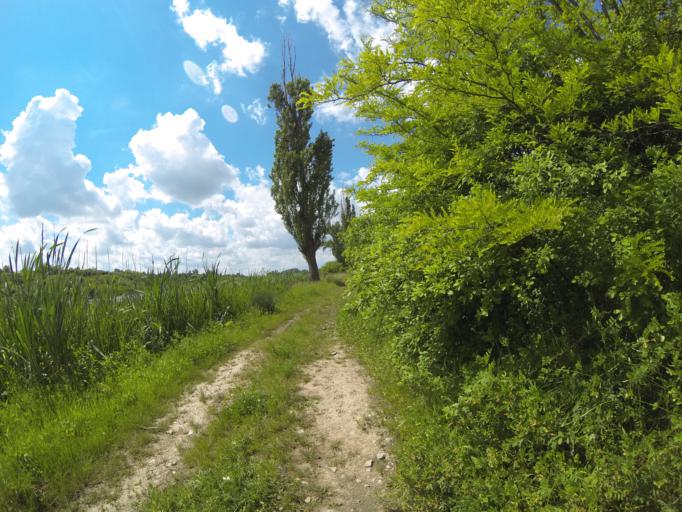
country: RO
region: Dolj
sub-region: Comuna Malu Mare
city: Preajba
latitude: 44.2666
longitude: 23.8546
